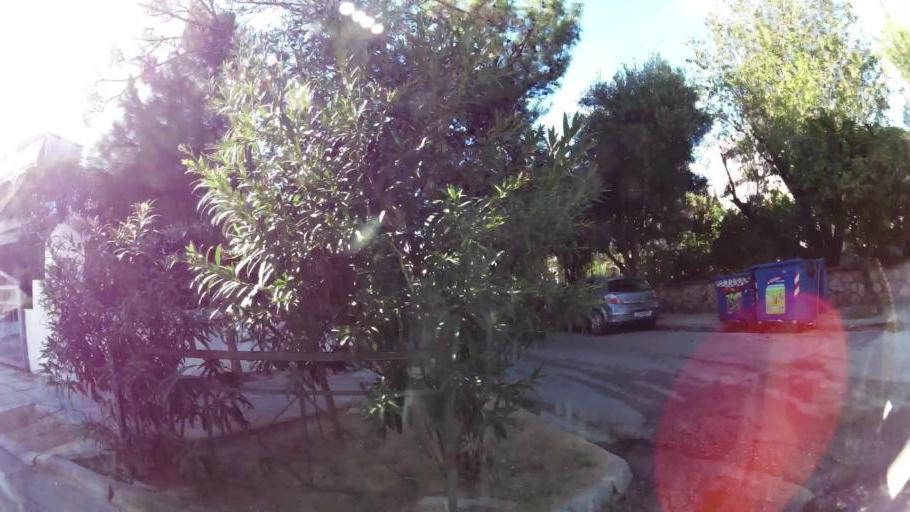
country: GR
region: Attica
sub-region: Nomarchia Athinas
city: Khalandrion
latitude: 38.0233
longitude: 23.8083
